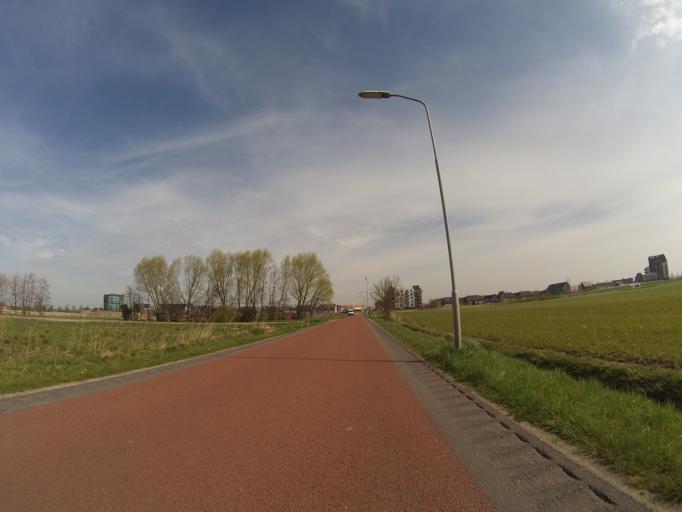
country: NL
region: Gelderland
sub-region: Gemeente Nijkerk
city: Nijkerk
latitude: 52.2089
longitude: 5.4547
